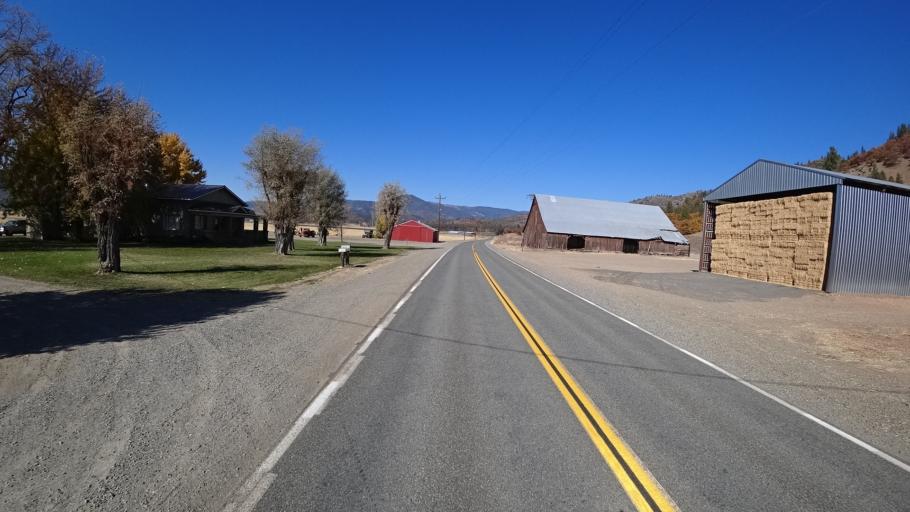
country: US
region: California
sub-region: Siskiyou County
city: Yreka
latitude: 41.6144
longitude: -122.8580
